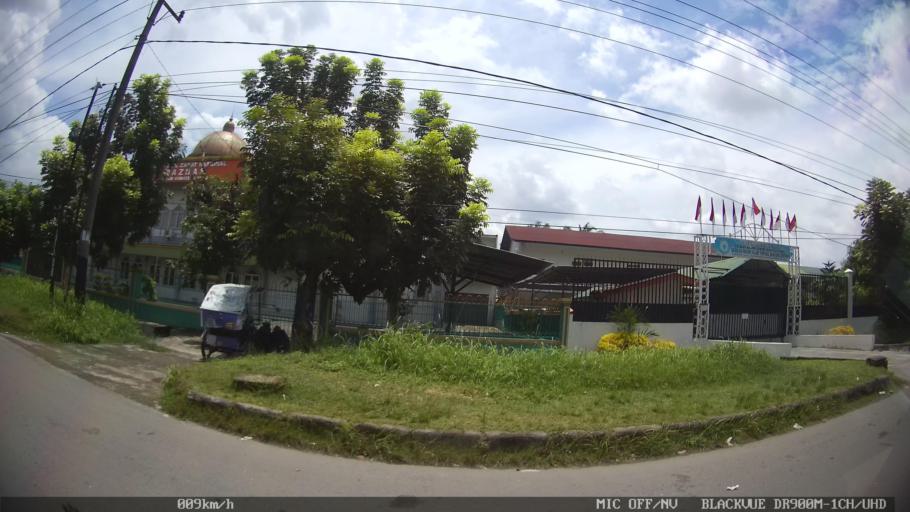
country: ID
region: North Sumatra
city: Medan
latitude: 3.6141
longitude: 98.7137
